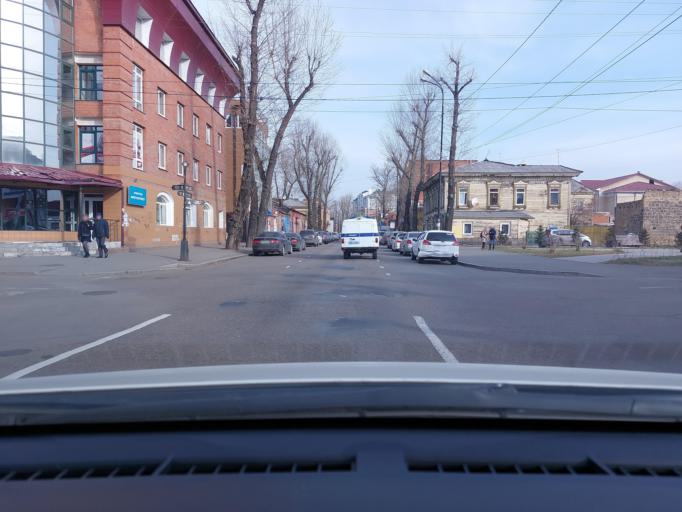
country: RU
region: Irkutsk
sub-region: Irkutskiy Rayon
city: Irkutsk
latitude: 52.2787
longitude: 104.2866
